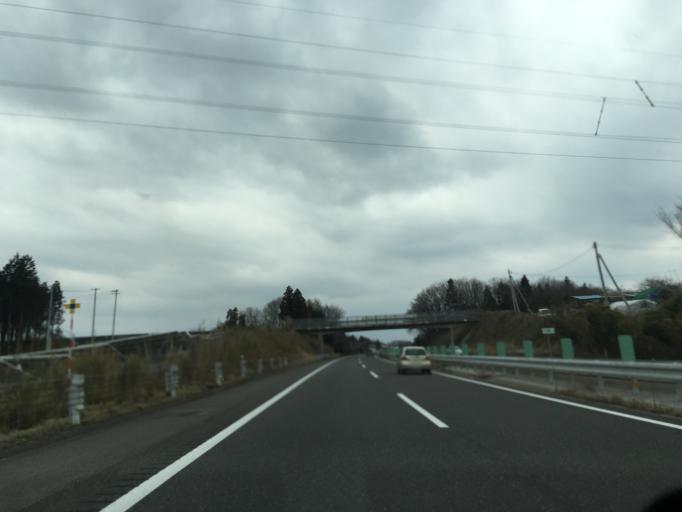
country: JP
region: Fukushima
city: Sukagawa
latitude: 37.2736
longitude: 140.3504
